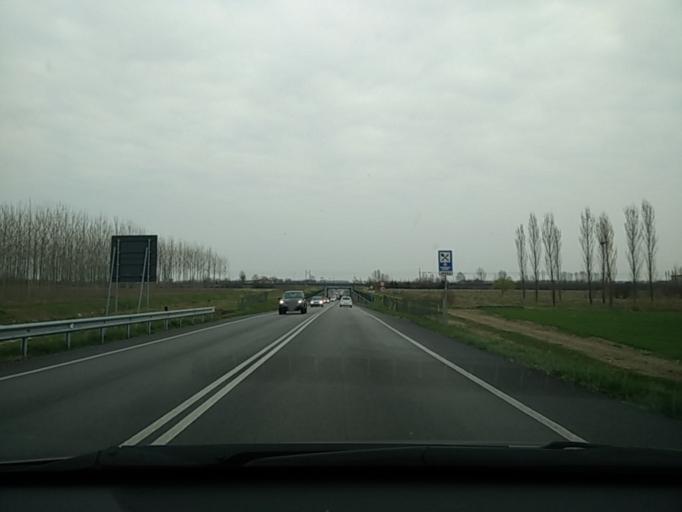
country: IT
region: Veneto
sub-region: Provincia di Venezia
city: San Dona di Piave
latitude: 45.6543
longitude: 12.5768
